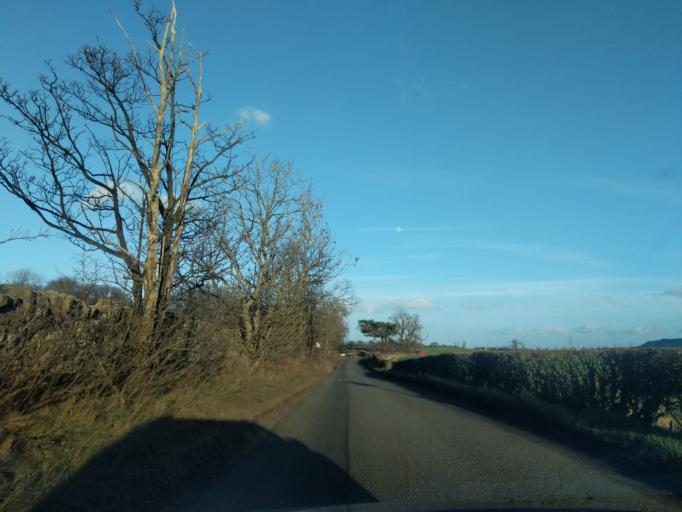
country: GB
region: Scotland
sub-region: Edinburgh
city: Balerno
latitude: 55.9007
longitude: -3.3461
